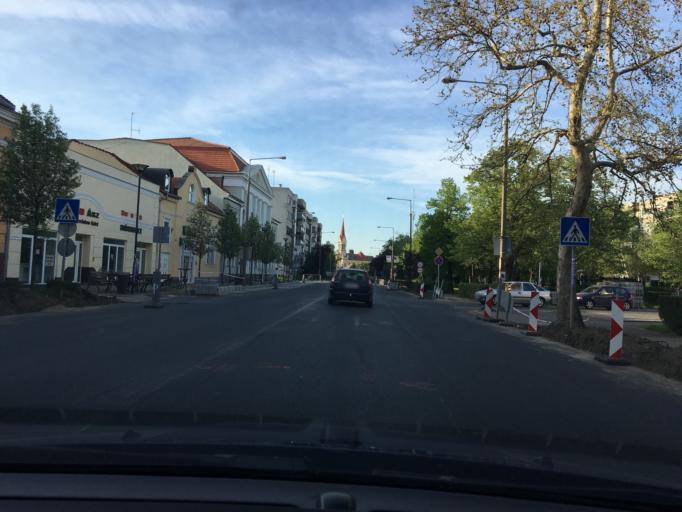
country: HU
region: Hajdu-Bihar
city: Berettyoujfalu
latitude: 47.2233
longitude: 21.5353
